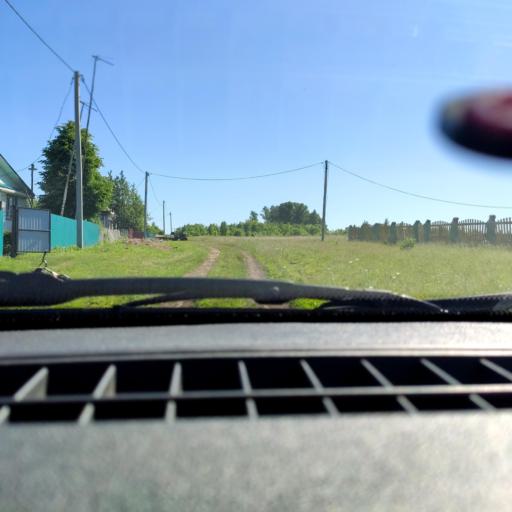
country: RU
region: Bashkortostan
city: Iglino
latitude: 54.8902
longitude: 56.4988
